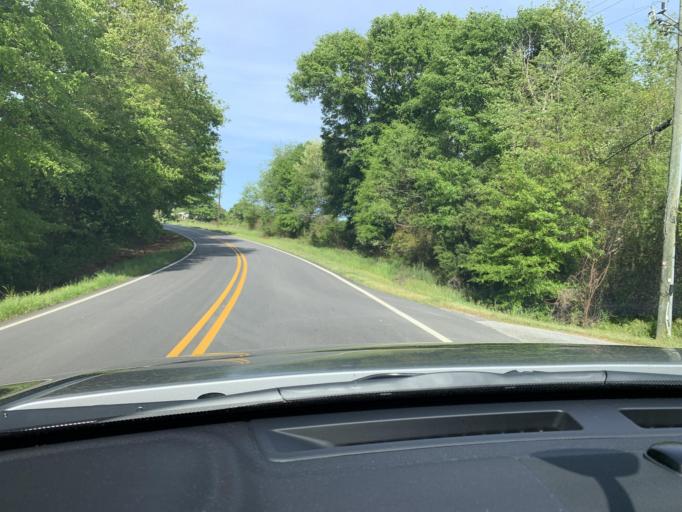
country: US
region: Georgia
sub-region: Oconee County
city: Watkinsville
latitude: 33.8174
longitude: -83.4302
